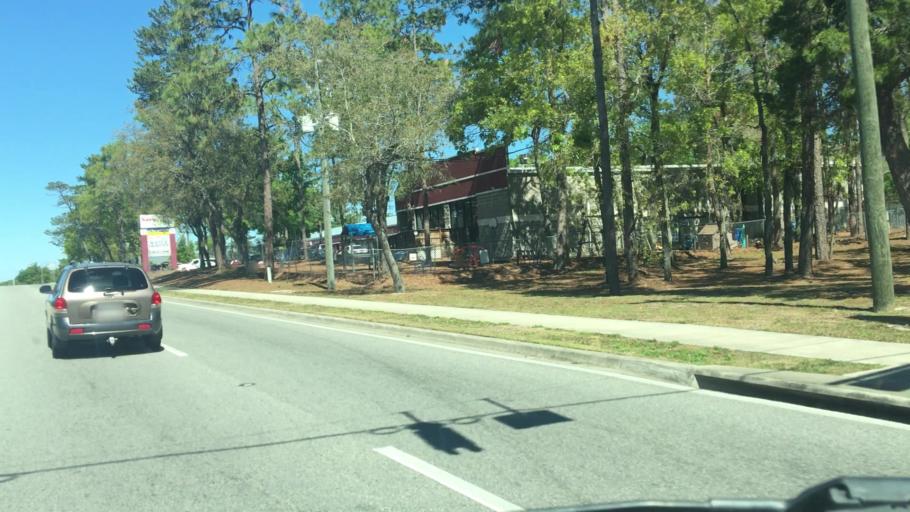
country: US
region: Florida
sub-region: Volusia County
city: Deltona
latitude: 28.9026
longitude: -81.1714
